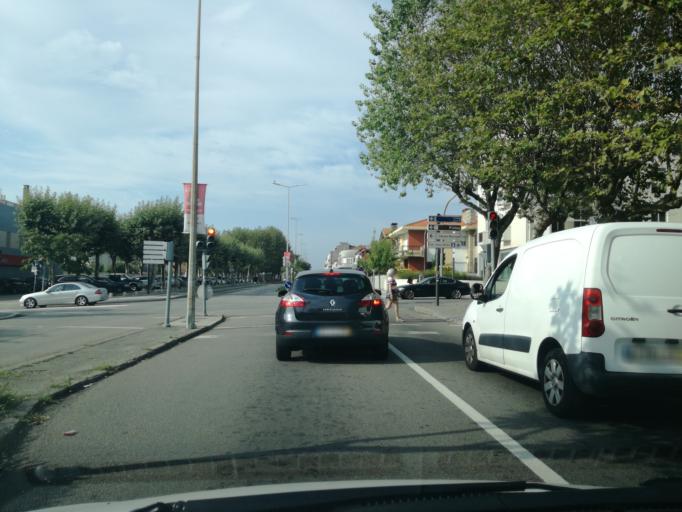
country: PT
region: Aveiro
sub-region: Espinho
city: Espinho
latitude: 41.0083
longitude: -8.6380
